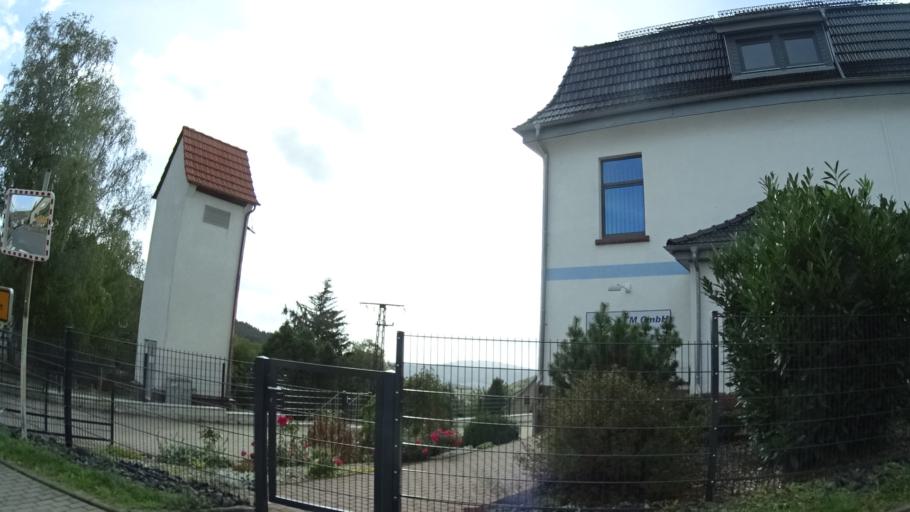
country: DE
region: Thuringia
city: Rotterode
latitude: 50.7113
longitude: 10.5493
